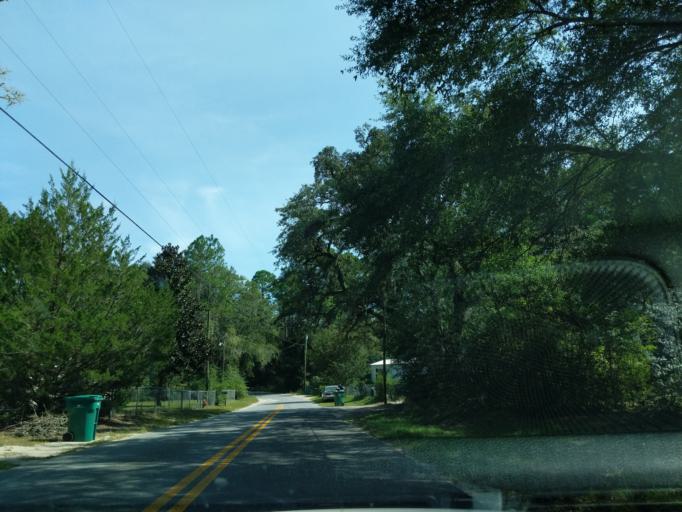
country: US
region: Florida
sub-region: Okaloosa County
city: Crestview
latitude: 30.7089
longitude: -86.5993
